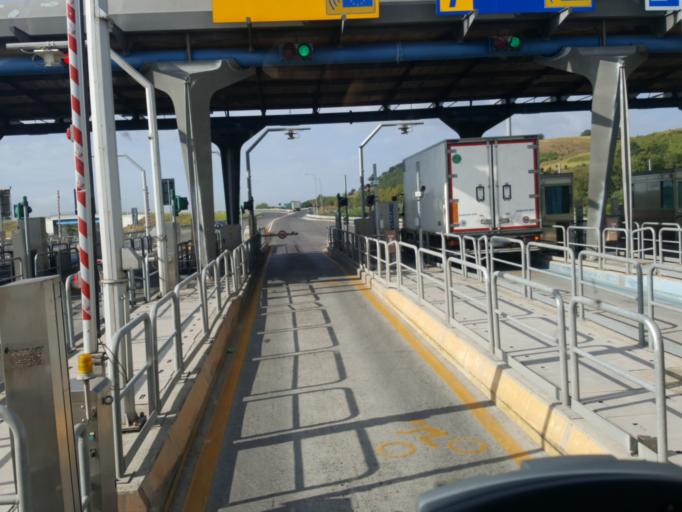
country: IT
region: Latium
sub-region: Citta metropolitana di Roma Capitale
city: Girardi-Bellavista-Terrazze
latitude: 42.0908
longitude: 12.5681
